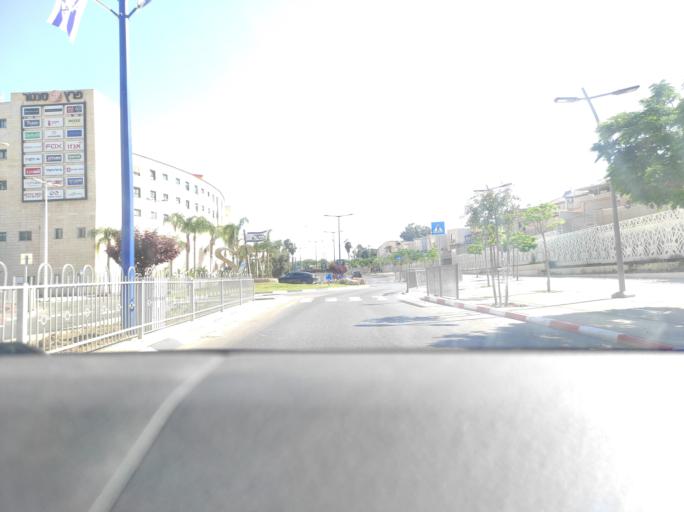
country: IL
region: Southern District
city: Sederot
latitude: 31.5223
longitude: 34.5943
